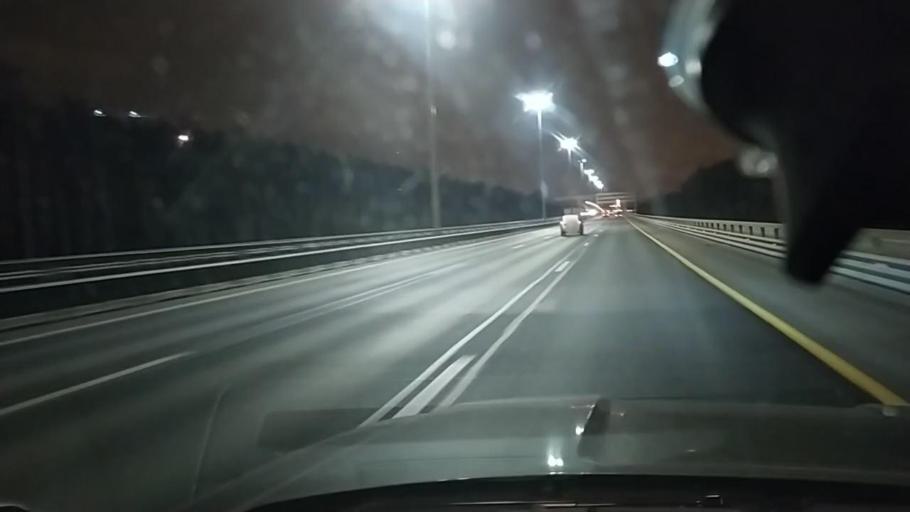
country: RU
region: Leningrad
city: Untolovo
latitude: 60.0319
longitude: 30.1932
